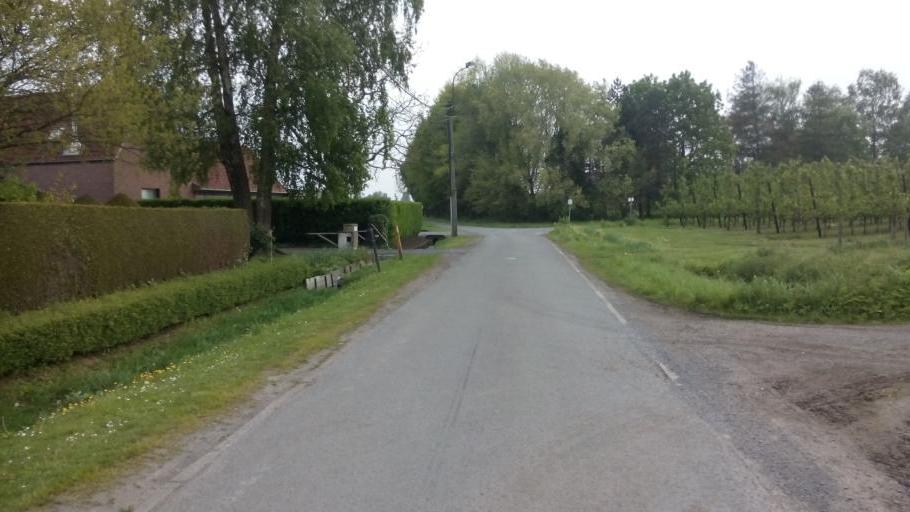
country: BE
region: Flanders
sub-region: Provincie Oost-Vlaanderen
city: Nevele
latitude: 51.0668
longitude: 3.5426
